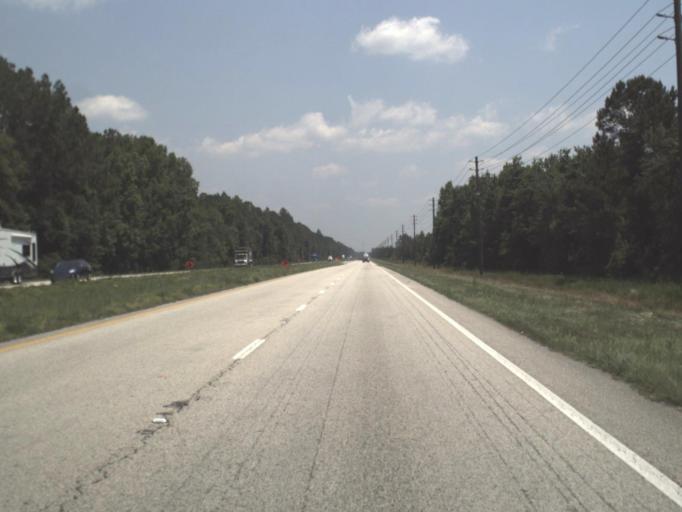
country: US
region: Florida
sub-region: Duval County
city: Baldwin
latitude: 30.2511
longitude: -81.9955
